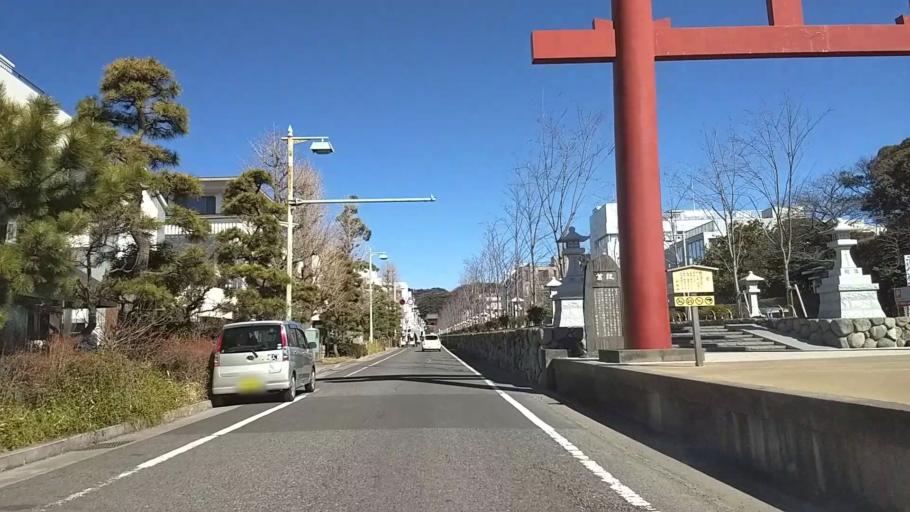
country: JP
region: Kanagawa
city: Kamakura
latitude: 35.3198
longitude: 139.5525
